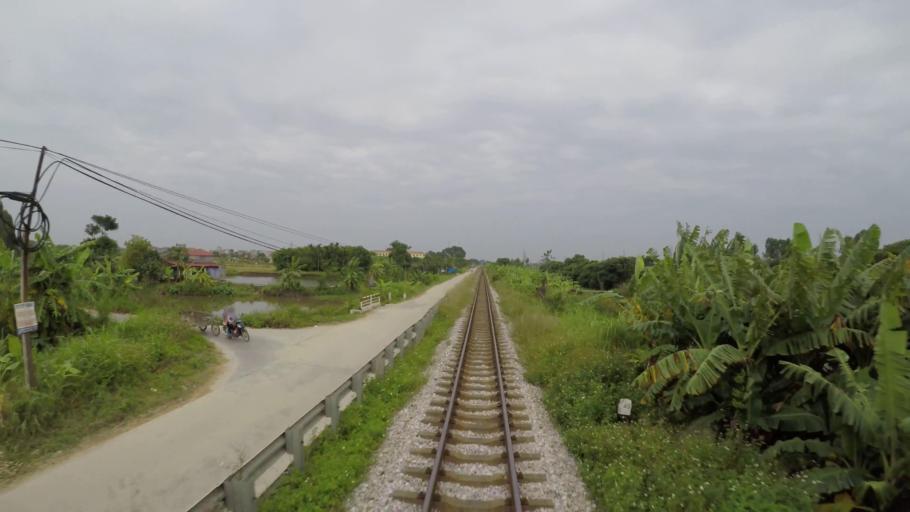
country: VN
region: Hai Duong
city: Lai Cach
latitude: 20.9510
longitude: 106.2390
